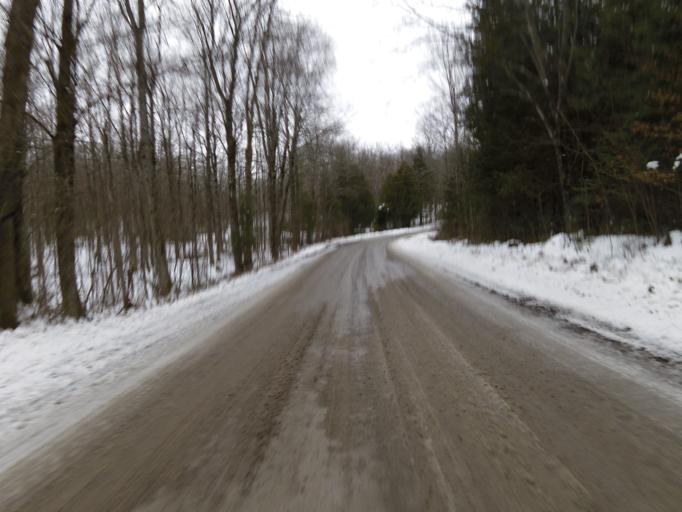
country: CA
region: Ontario
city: Carleton Place
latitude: 45.1690
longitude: -76.2334
